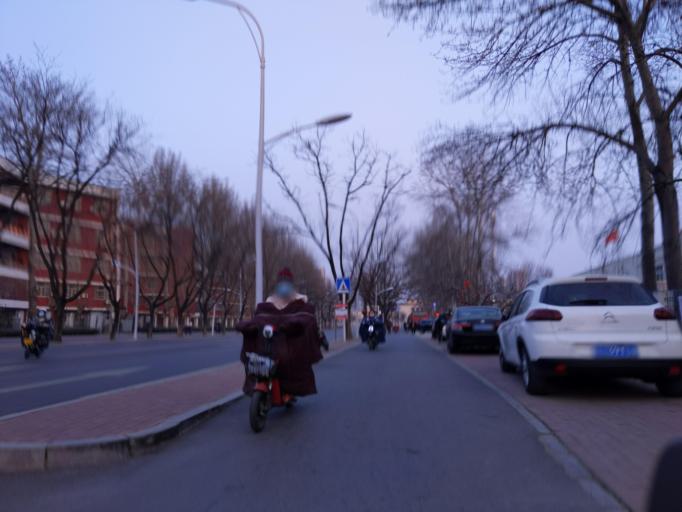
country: CN
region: Henan Sheng
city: Zhongyuanlu
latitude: 35.7690
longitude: 115.0962
